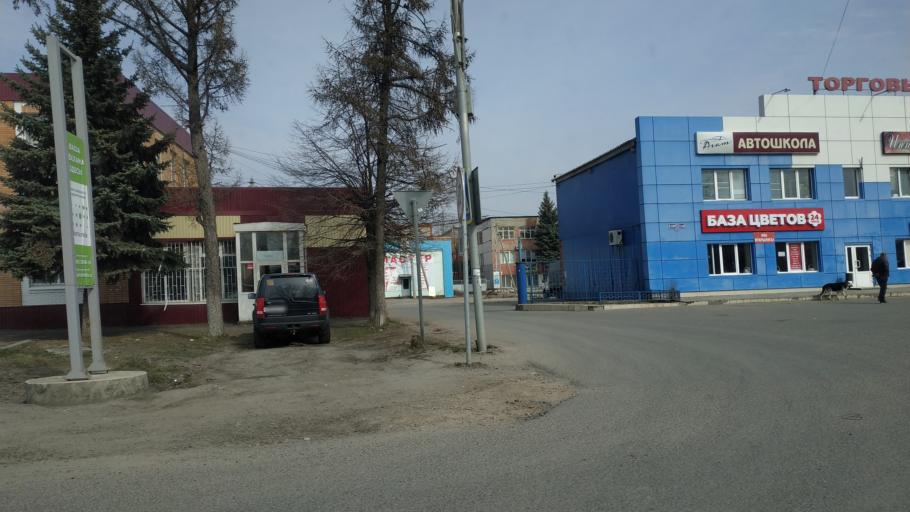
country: RU
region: Moskovskaya
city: Bronnitsy
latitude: 55.4146
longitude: 38.2855
